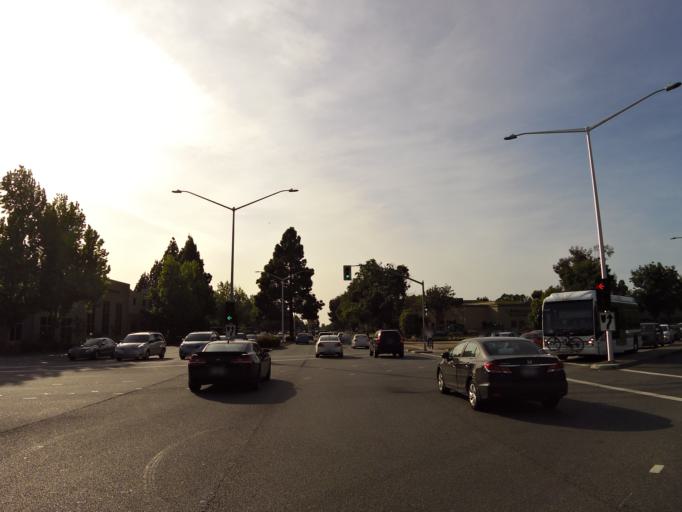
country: US
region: California
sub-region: Alameda County
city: Fremont
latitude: 37.5490
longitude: -121.9721
